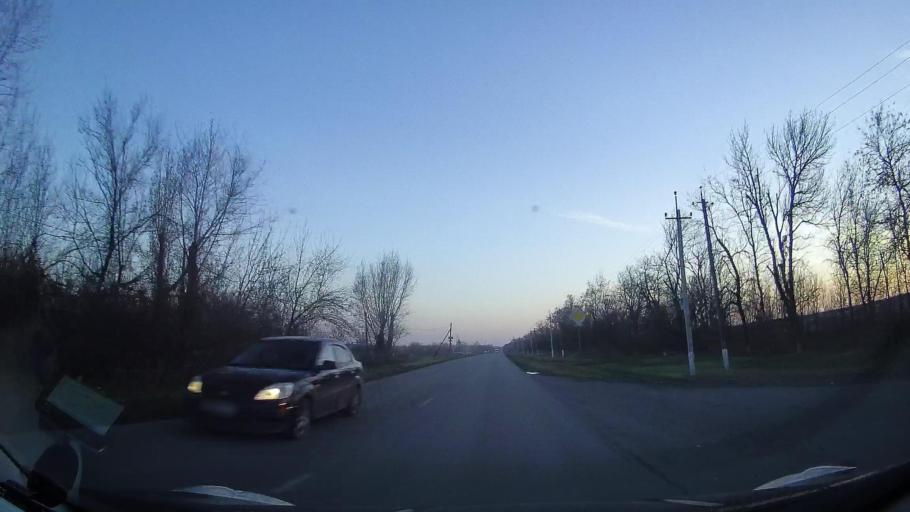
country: RU
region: Rostov
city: Zernograd
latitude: 47.0488
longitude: 40.3915
